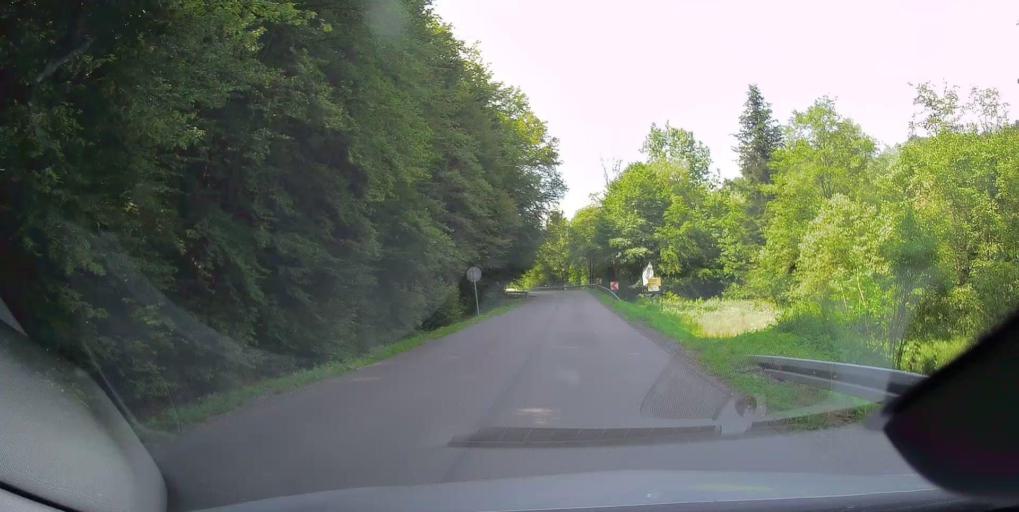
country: PL
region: Lesser Poland Voivodeship
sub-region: Powiat tarnowski
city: Zakliczyn
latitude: 49.7807
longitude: 20.7840
